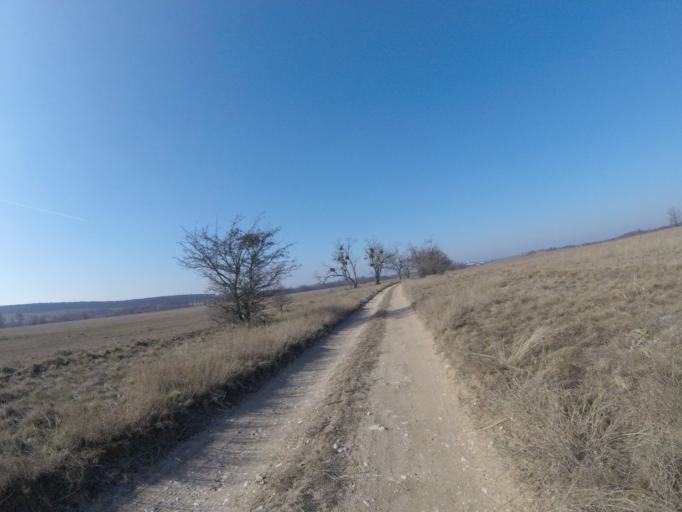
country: HU
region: Komarom-Esztergom
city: Oroszlany
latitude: 47.4640
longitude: 18.3451
